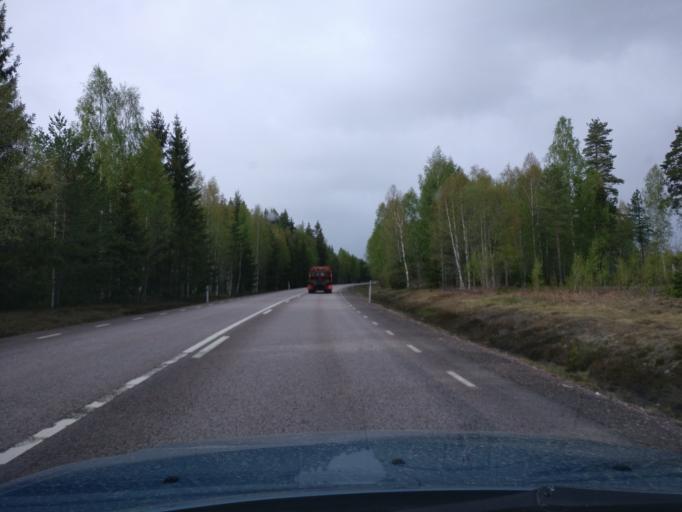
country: SE
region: Vaermland
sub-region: Forshaga Kommun
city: Deje
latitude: 59.6081
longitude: 13.4464
